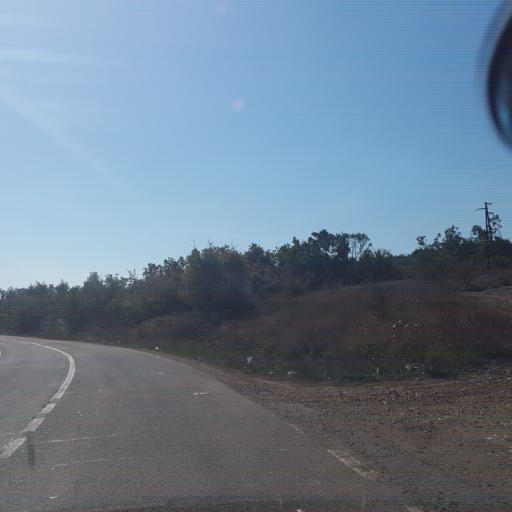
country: RS
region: Central Serbia
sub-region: Nisavski Okrug
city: Svrljig
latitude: 43.4635
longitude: 22.2109
